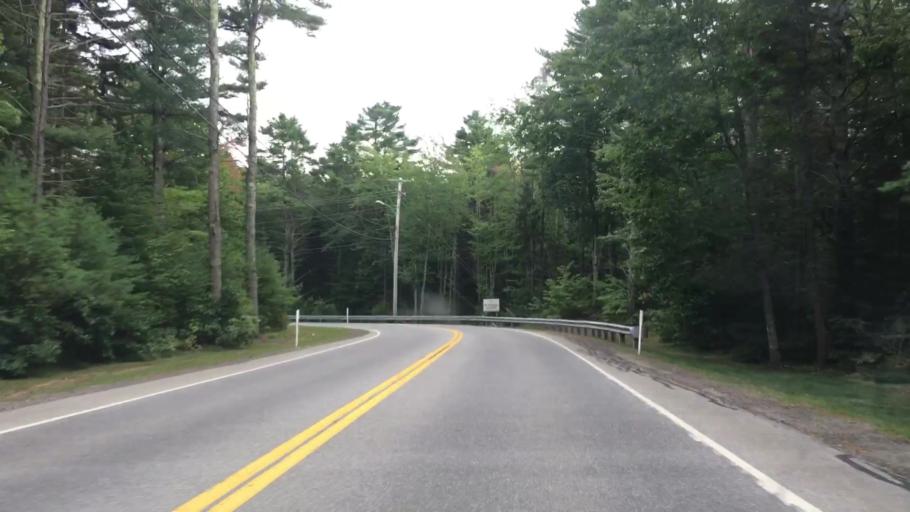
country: US
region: Maine
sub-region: Cumberland County
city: Brunswick
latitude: 43.9094
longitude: -69.8966
